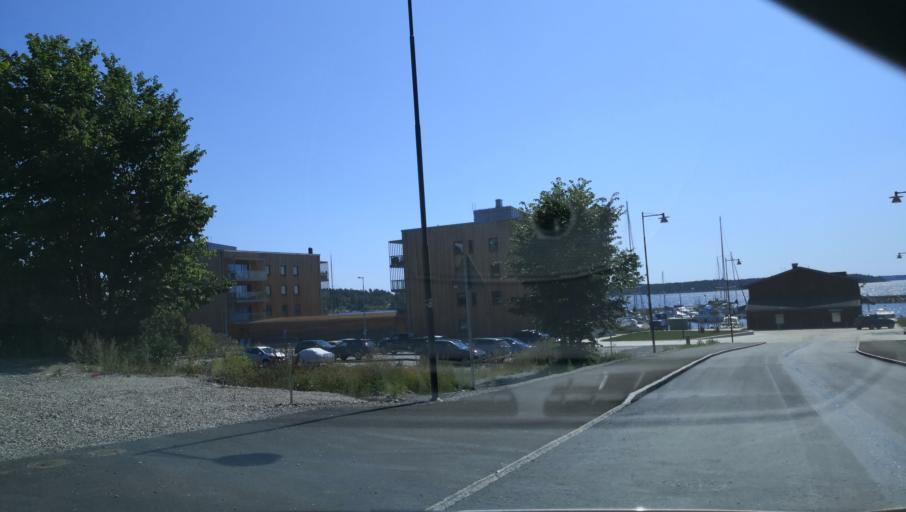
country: SE
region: Stockholm
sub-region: Varmdo Kommun
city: Mortnas
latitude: 59.3936
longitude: 18.4367
